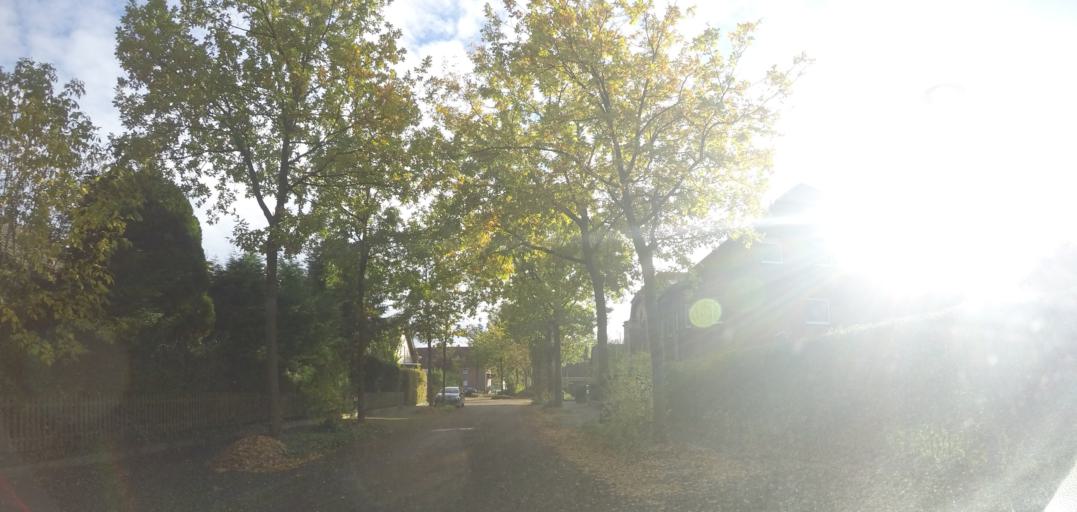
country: DE
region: North Rhine-Westphalia
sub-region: Regierungsbezirk Arnsberg
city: Lippstadt
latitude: 51.6585
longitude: 8.3252
